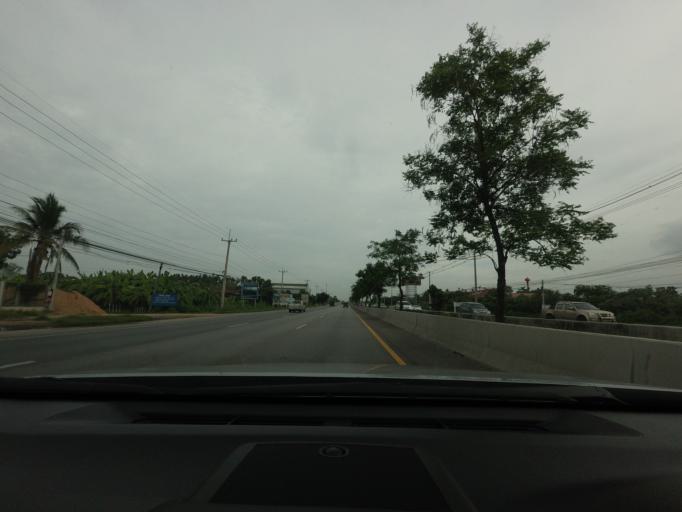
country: TH
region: Phetchaburi
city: Tha Yang
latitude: 12.9123
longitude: 99.9080
